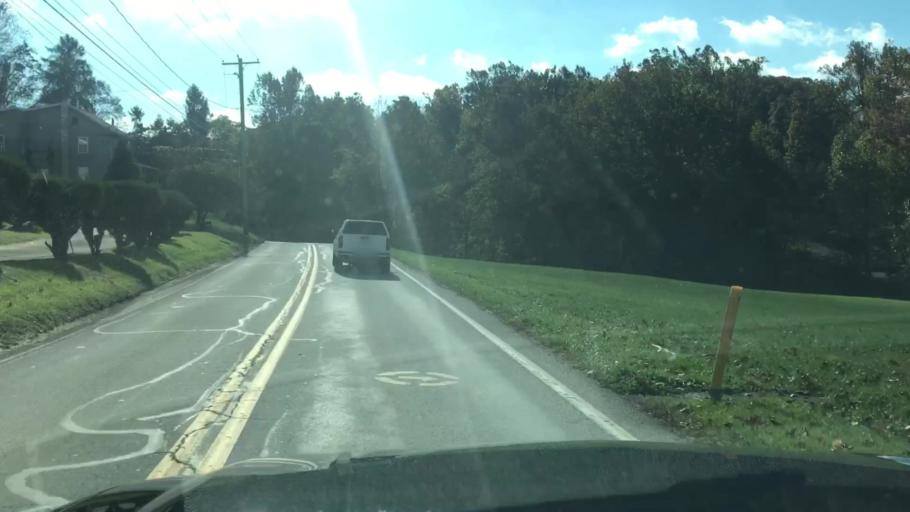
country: US
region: Pennsylvania
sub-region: Cumberland County
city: Lower Allen
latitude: 40.1893
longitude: -76.8898
